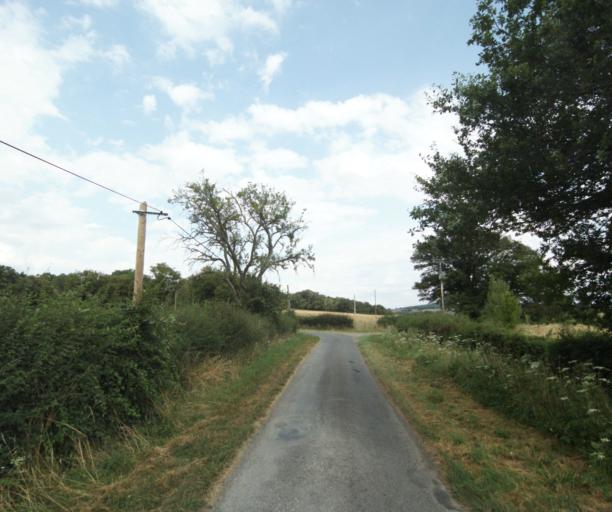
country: FR
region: Bourgogne
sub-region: Departement de Saone-et-Loire
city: Gueugnon
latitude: 46.6109
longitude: 4.0834
